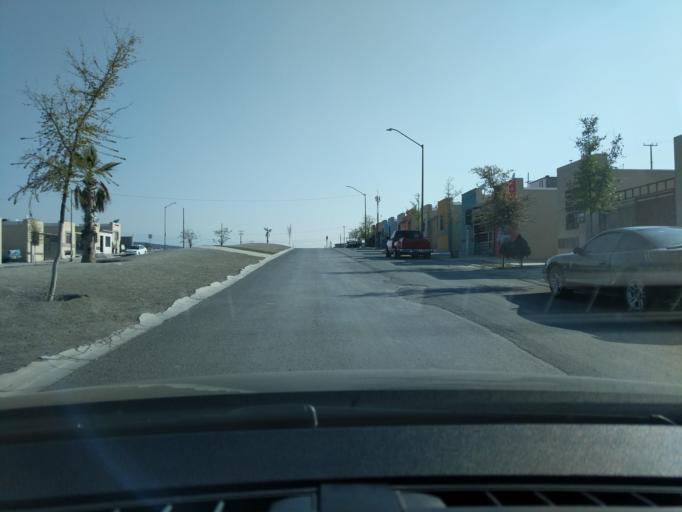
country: MX
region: Coahuila
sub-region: Ramos Arizpe
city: Ramos Arizpe
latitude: 25.5493
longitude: -100.9669
